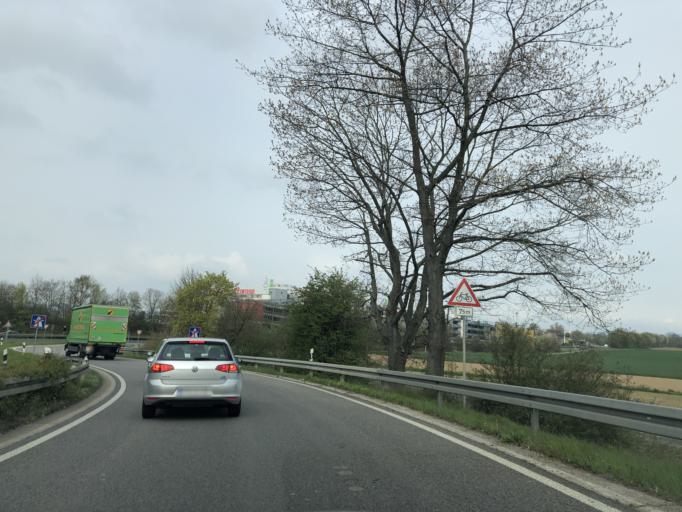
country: DE
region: Hesse
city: Sulzbach
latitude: 50.1165
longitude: 8.5338
